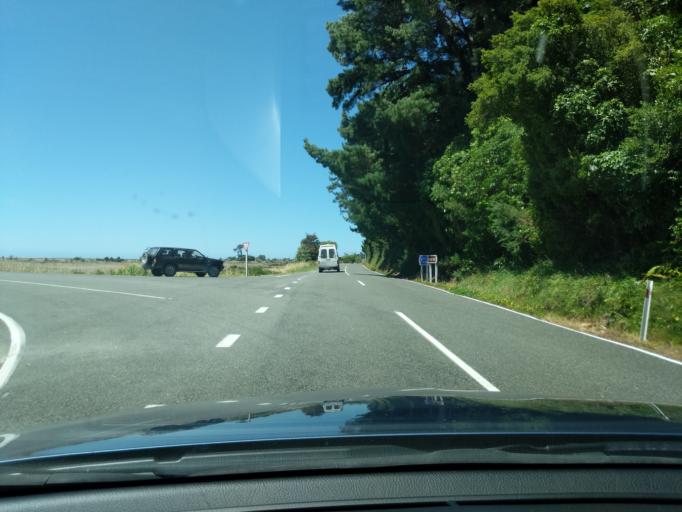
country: NZ
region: Tasman
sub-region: Tasman District
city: Takaka
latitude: -40.6818
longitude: 172.6671
